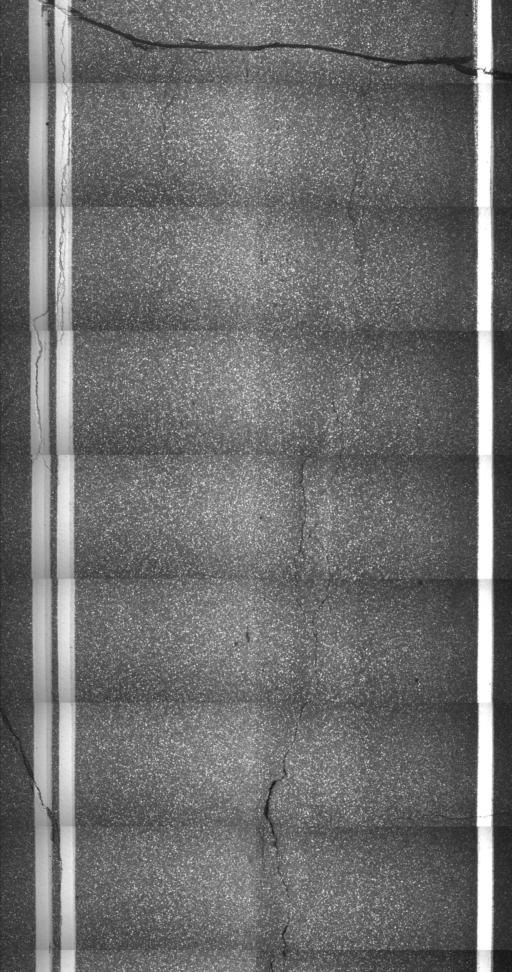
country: US
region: Vermont
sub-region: Washington County
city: Barre
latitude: 44.2827
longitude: -72.4378
